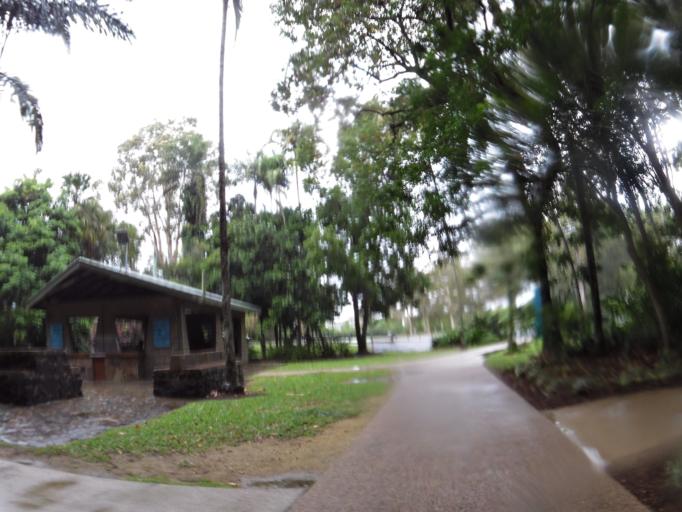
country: AU
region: Queensland
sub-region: Cairns
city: Cairns
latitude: -16.9033
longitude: 145.7502
